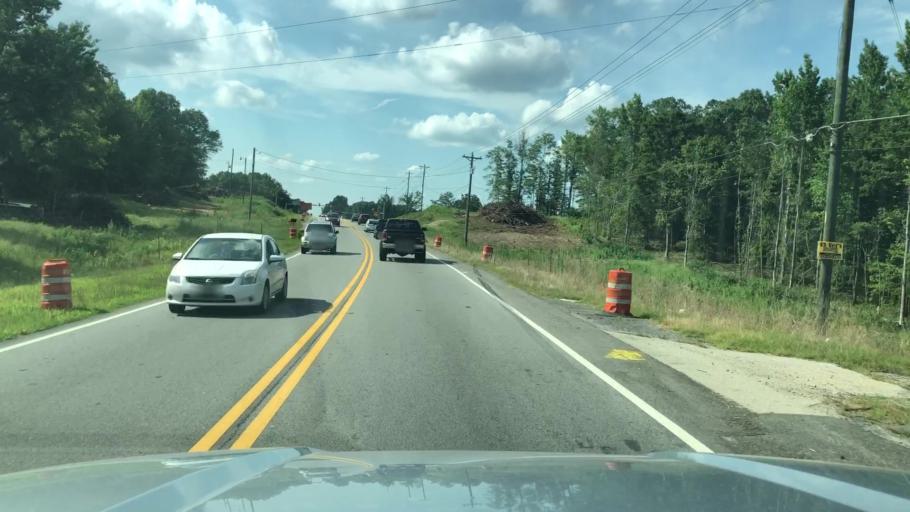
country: US
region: Georgia
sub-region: Paulding County
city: Hiram
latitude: 33.8537
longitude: -84.7568
